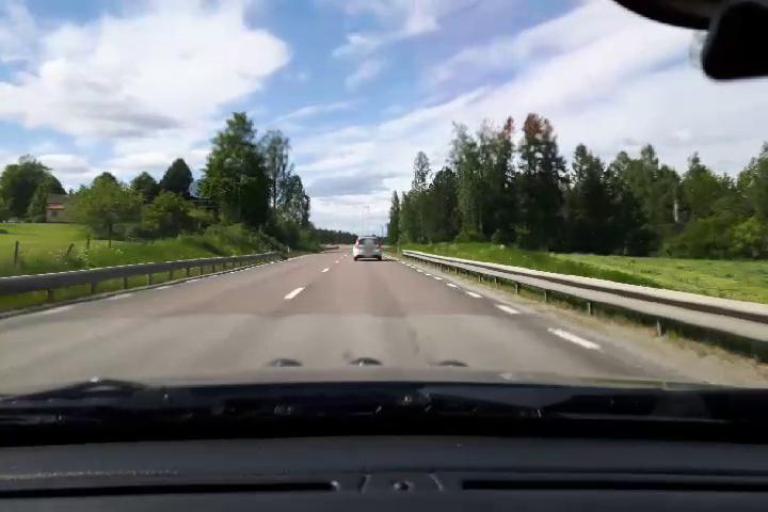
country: SE
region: Gaevleborg
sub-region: Bollnas Kommun
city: Bollnas
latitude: 61.3166
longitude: 16.4387
